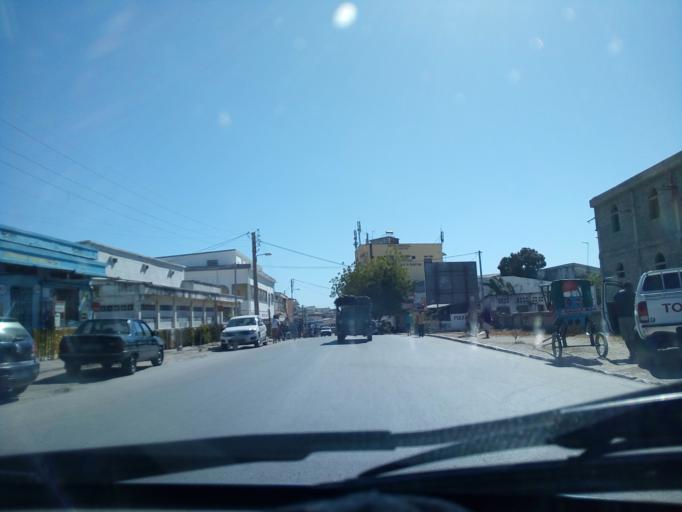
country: MG
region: Boeny
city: Mahajanga
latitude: -15.7140
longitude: 46.3182
